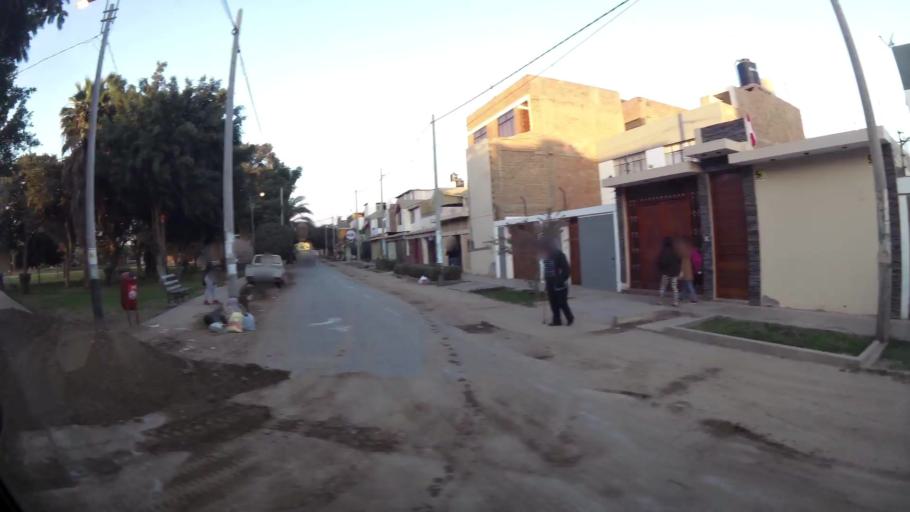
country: PE
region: Ica
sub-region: Provincia de Ica
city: Ica
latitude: -14.0777
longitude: -75.7286
